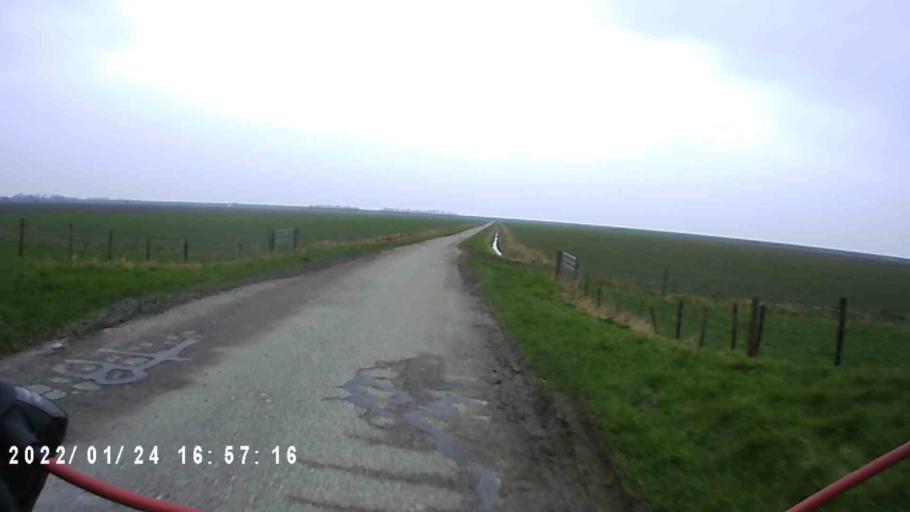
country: NL
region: Groningen
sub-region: Gemeente De Marne
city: Ulrum
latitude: 53.3863
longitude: 6.3366
